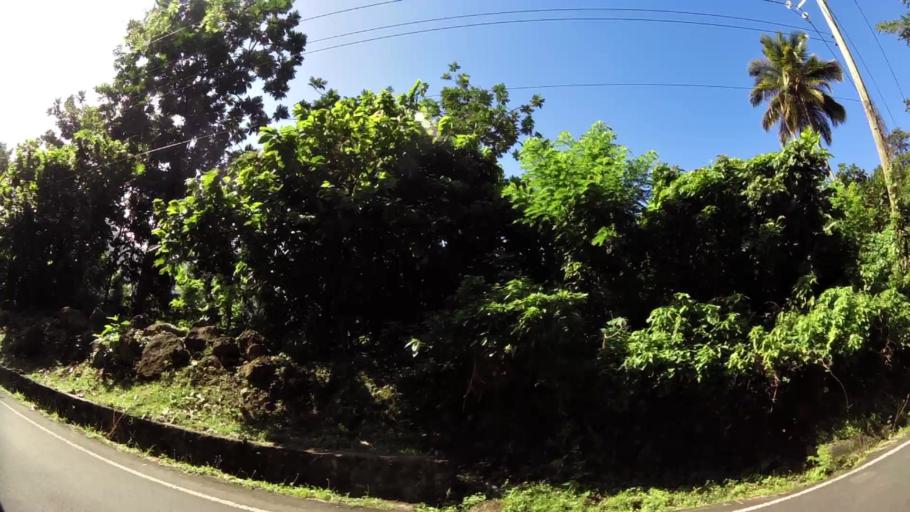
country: LC
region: Soufriere
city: Soufriere
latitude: 13.8645
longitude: -61.0511
